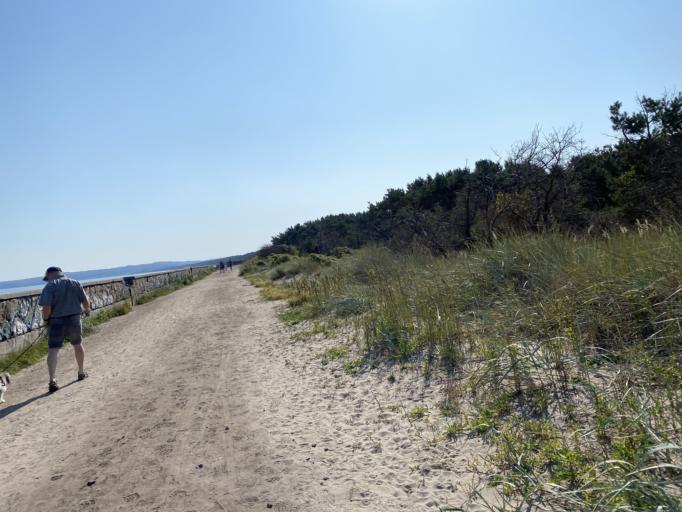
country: DE
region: Mecklenburg-Vorpommern
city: Ostseebad Binz
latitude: 54.4421
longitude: 13.5770
